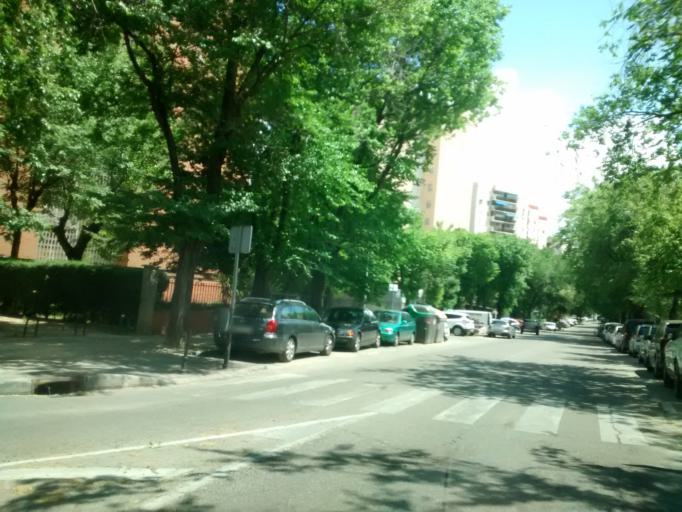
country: ES
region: Madrid
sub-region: Provincia de Madrid
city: San Fernando de Henares
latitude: 40.4311
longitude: -3.5426
